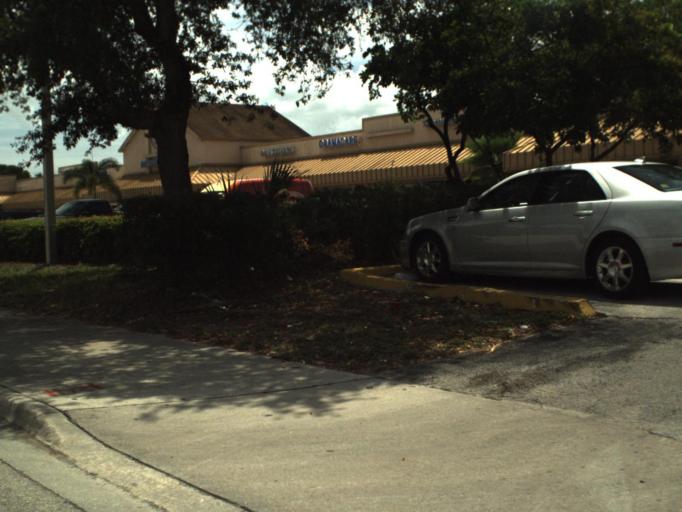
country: US
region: Florida
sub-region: Broward County
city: Margate
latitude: 26.2352
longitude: -80.2131
